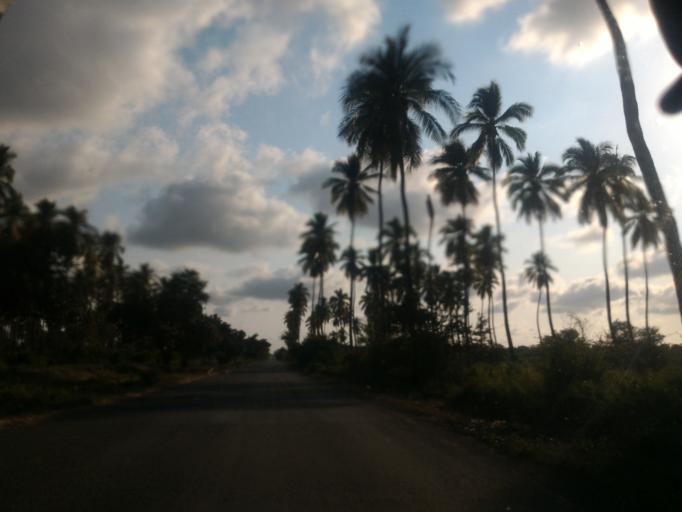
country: MX
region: Colima
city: Tecoman
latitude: 18.9064
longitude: -103.8555
